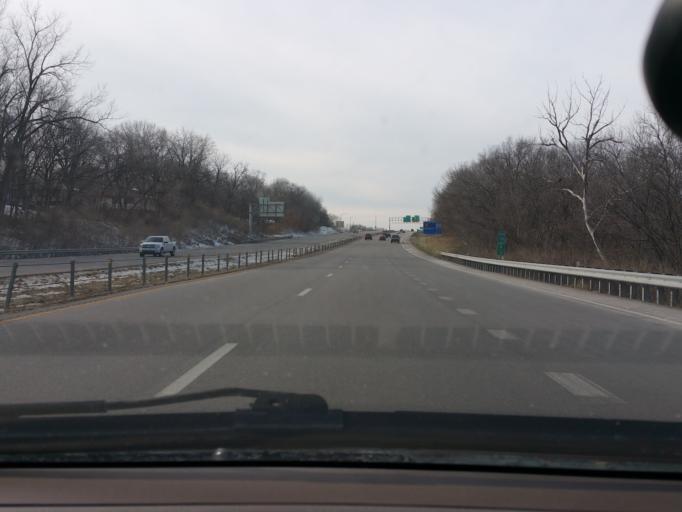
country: US
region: Missouri
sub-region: Clay County
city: Gladstone
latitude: 39.1734
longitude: -94.5413
